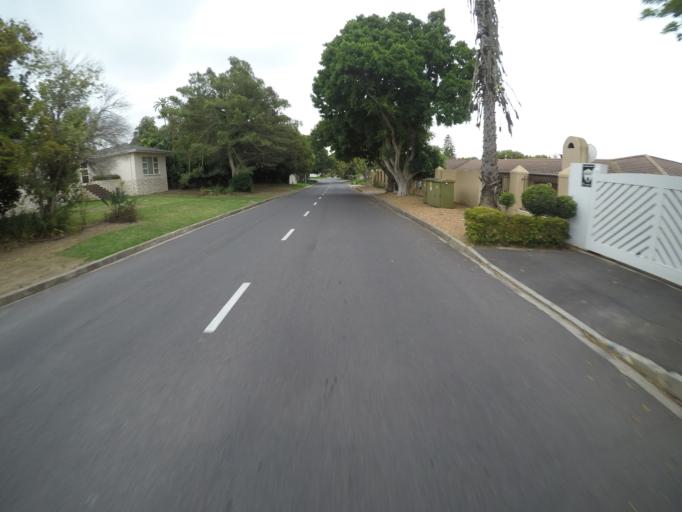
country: ZA
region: Western Cape
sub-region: City of Cape Town
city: Kraaifontein
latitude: -33.8646
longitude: 18.6479
